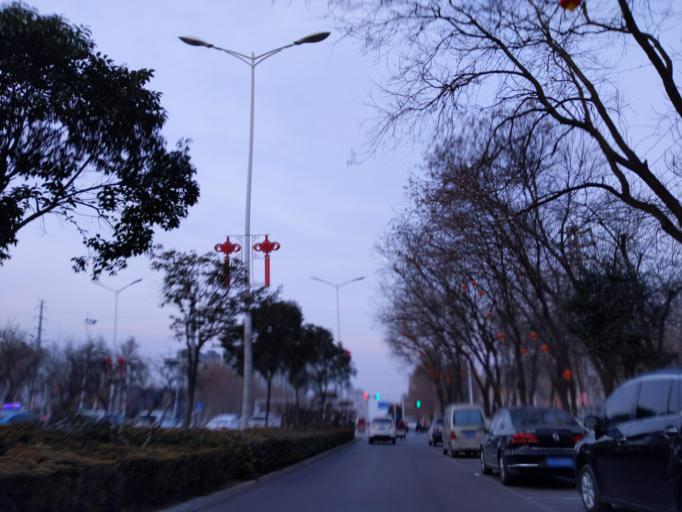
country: CN
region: Henan Sheng
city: Puyang
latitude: 35.7802
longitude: 115.0207
